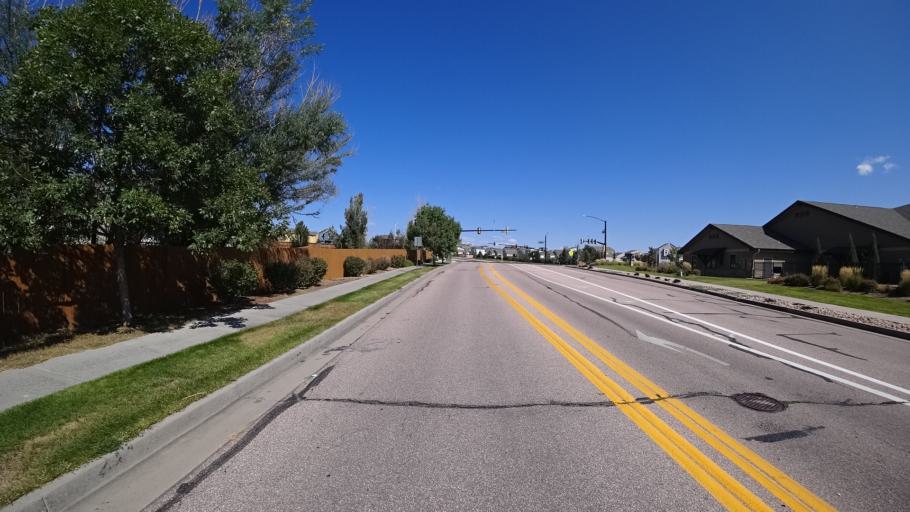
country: US
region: Colorado
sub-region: El Paso County
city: Cimarron Hills
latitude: 38.9253
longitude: -104.6995
